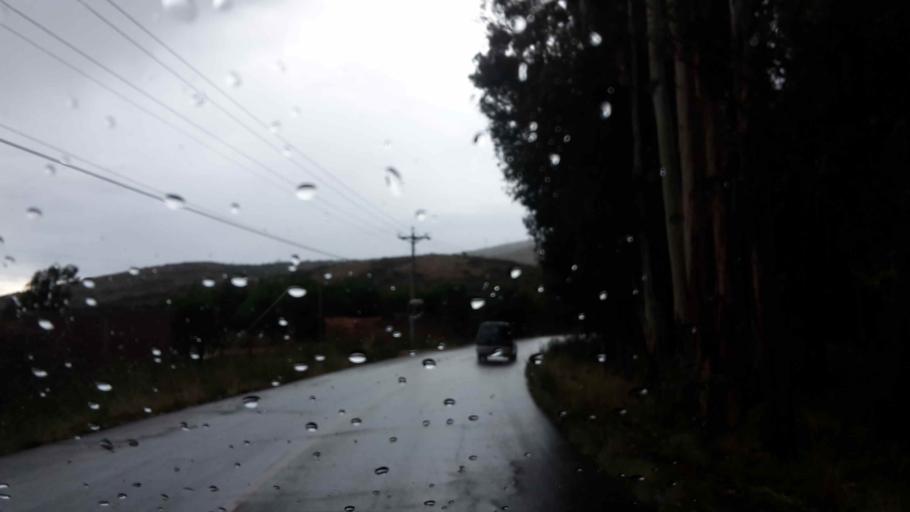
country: BO
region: Cochabamba
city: Tarata
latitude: -17.5401
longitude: -66.1157
